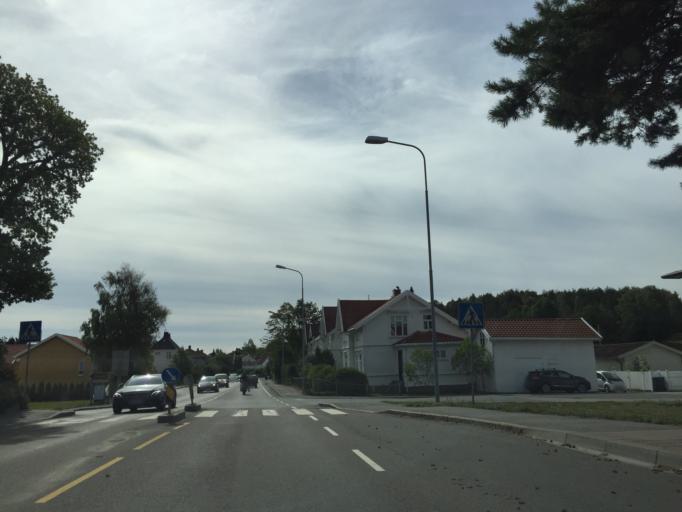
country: NO
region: Ostfold
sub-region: Fredrikstad
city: Fredrikstad
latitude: 59.2041
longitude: 10.9382
